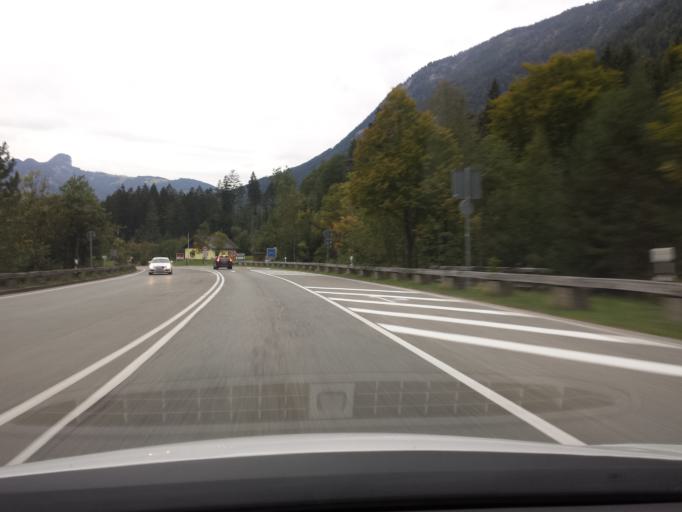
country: AT
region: Salzburg
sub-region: Politischer Bezirk Zell am See
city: Unken
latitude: 47.6671
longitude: 12.7555
